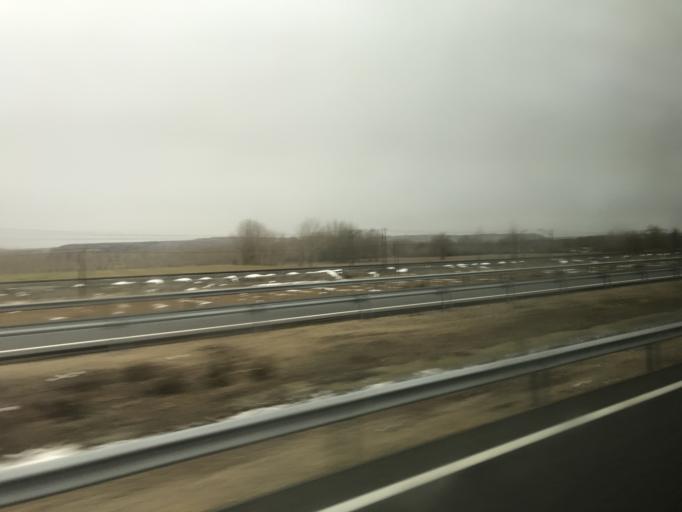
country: ES
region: Castille and Leon
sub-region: Provincia de Burgos
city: Villaverde-Mogina
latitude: 42.1832
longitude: -4.0447
